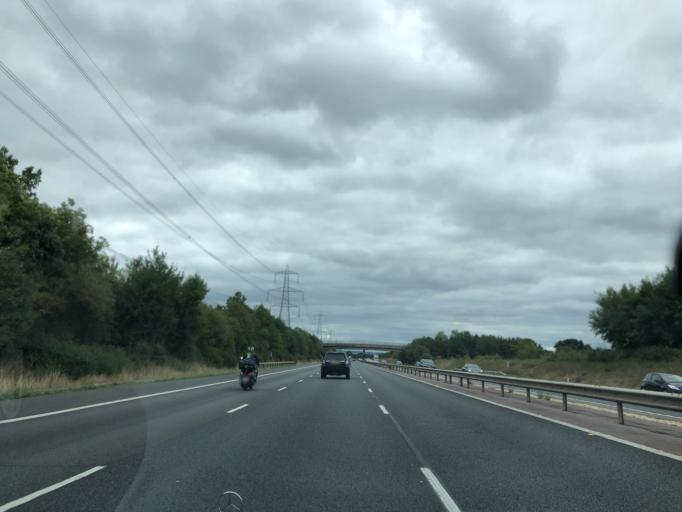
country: GB
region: England
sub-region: Oxfordshire
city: Wheatley
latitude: 51.8014
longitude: -1.0926
